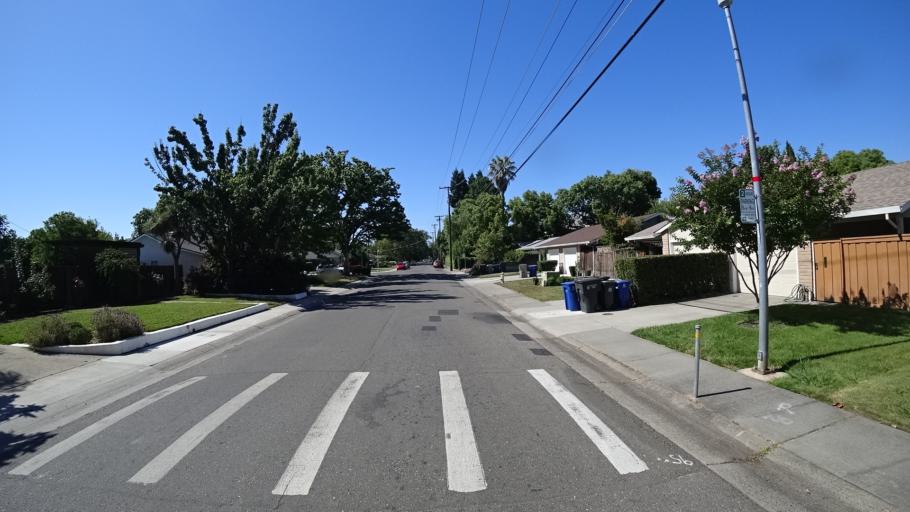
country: US
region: California
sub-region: Sacramento County
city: Parkway
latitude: 38.5457
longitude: -121.4440
